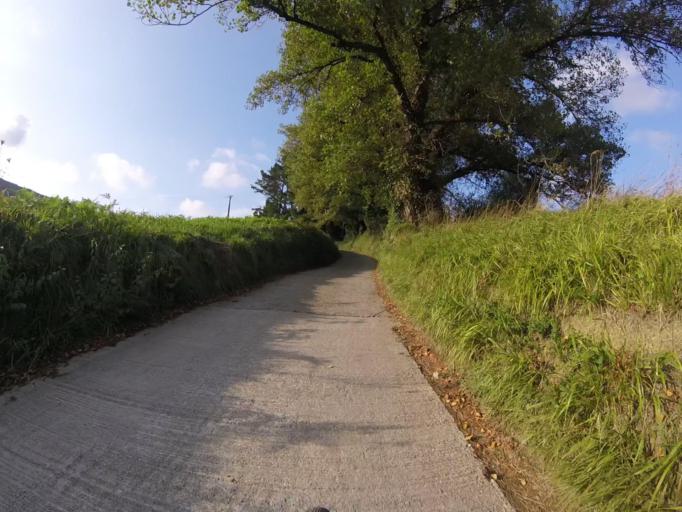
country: ES
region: Basque Country
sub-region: Provincia de Guipuzcoa
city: Fuenterrabia
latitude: 43.3558
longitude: -1.8121
